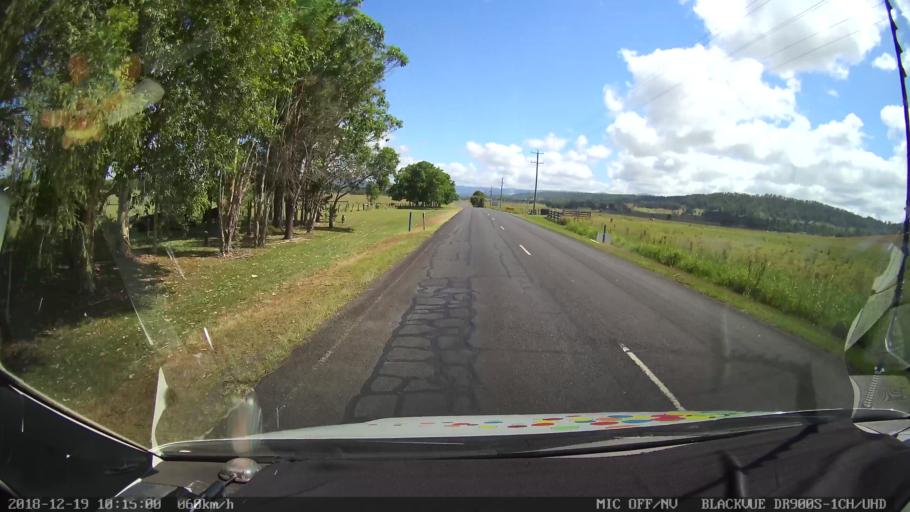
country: AU
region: New South Wales
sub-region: Kyogle
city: Kyogle
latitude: -28.6092
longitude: 153.0104
